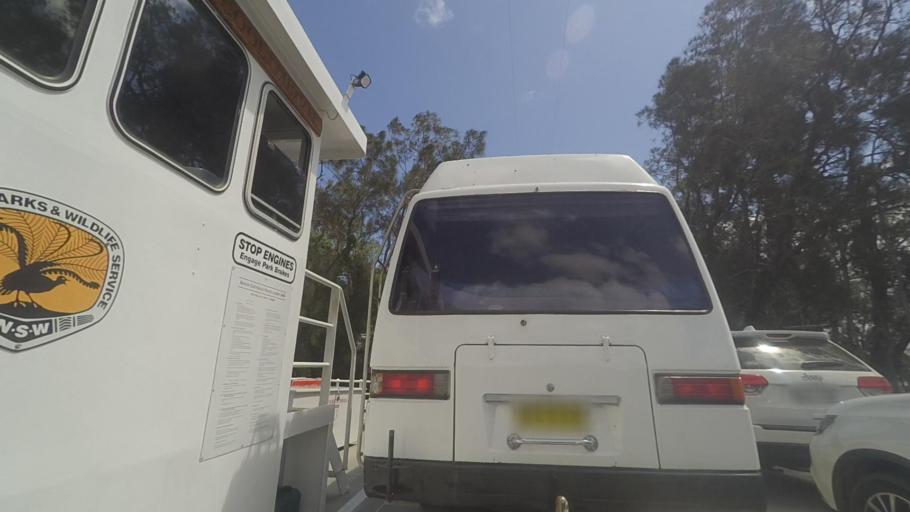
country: AU
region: New South Wales
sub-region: Great Lakes
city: Bulahdelah
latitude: -32.5047
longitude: 152.3044
